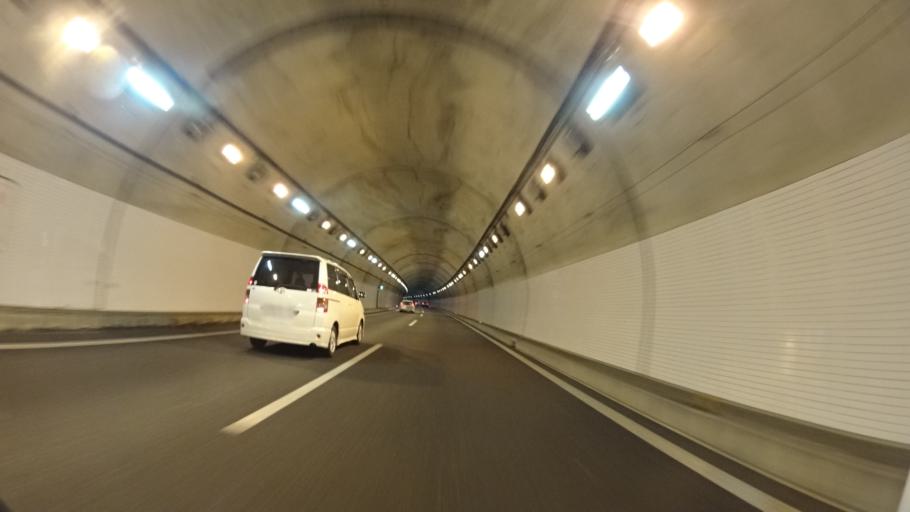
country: JP
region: Ehime
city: Saijo
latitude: 33.8925
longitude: 133.1977
